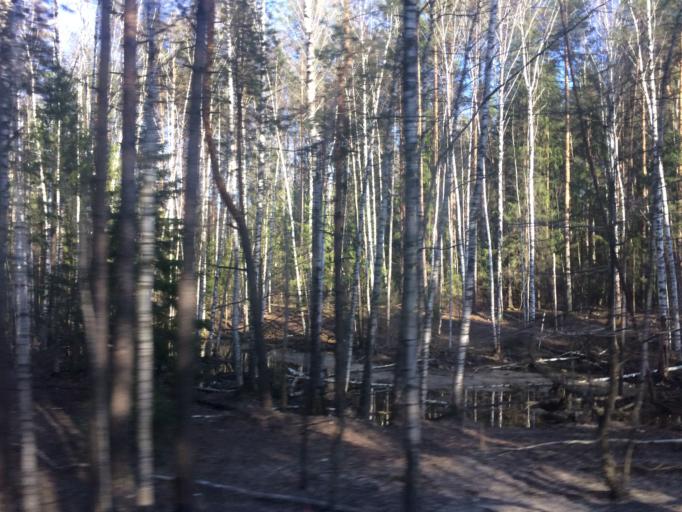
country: RU
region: Tatarstan
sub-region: Zelenodol'skiy Rayon
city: Vasil'yevo
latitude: 55.8939
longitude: 48.7286
